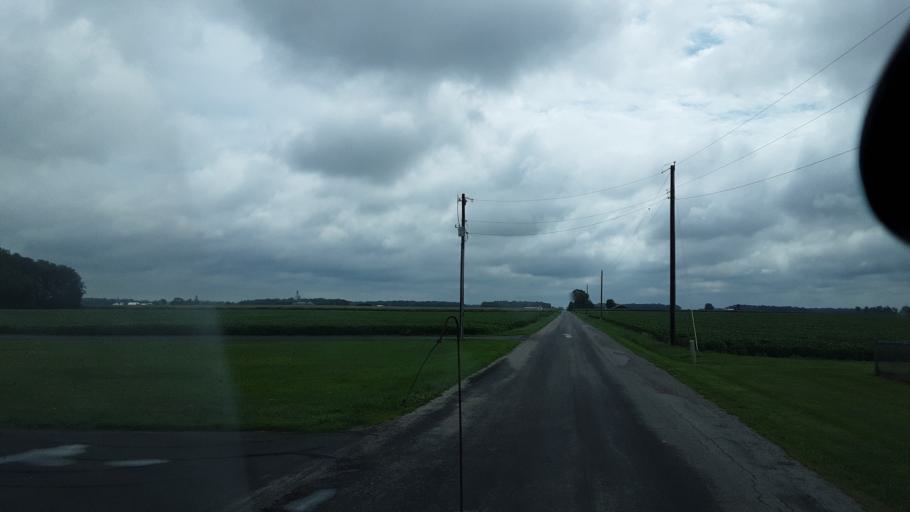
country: US
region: Indiana
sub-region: Wells County
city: Ossian
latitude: 40.8521
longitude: -85.1004
